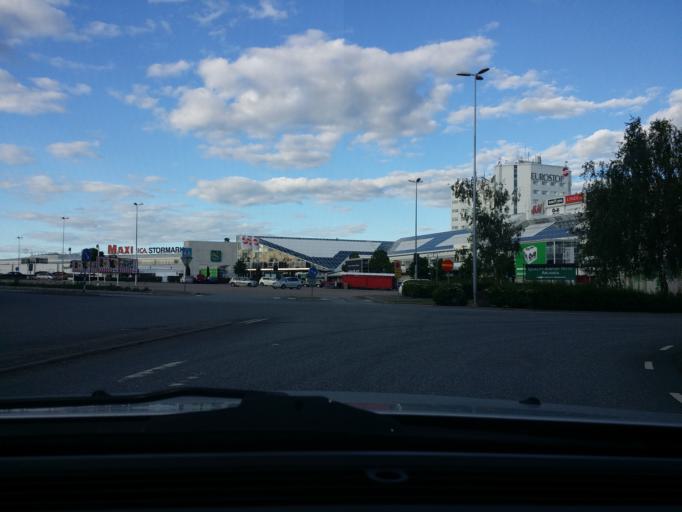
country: SE
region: Stockholm
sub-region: Sigtuna Kommun
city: Rosersberg
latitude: 59.6074
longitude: 17.8946
